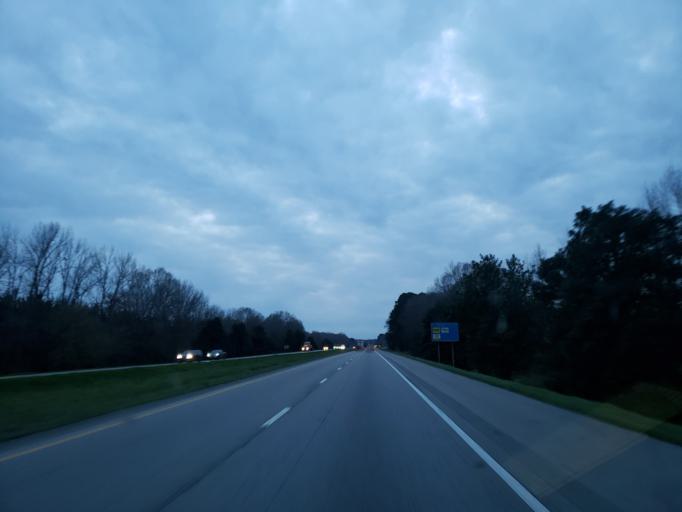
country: US
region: Mississippi
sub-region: Lauderdale County
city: Marion
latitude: 32.4137
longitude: -88.4970
